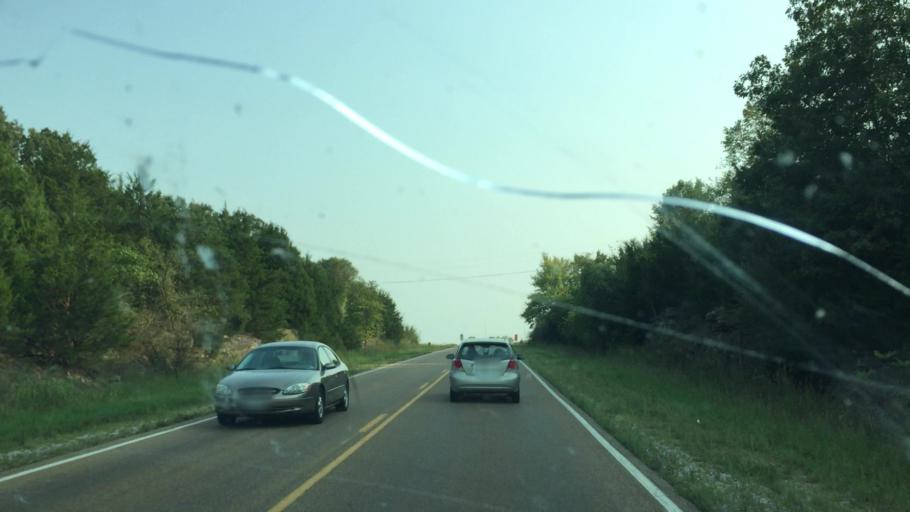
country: US
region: Missouri
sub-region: Pulaski County
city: Richland
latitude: 37.8143
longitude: -92.4071
